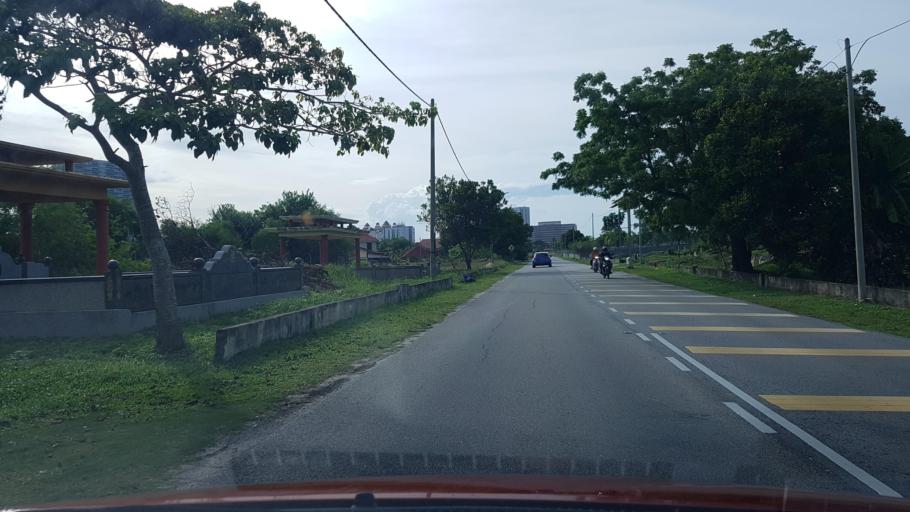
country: MY
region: Terengganu
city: Kuala Terengganu
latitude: 5.3192
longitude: 103.1474
